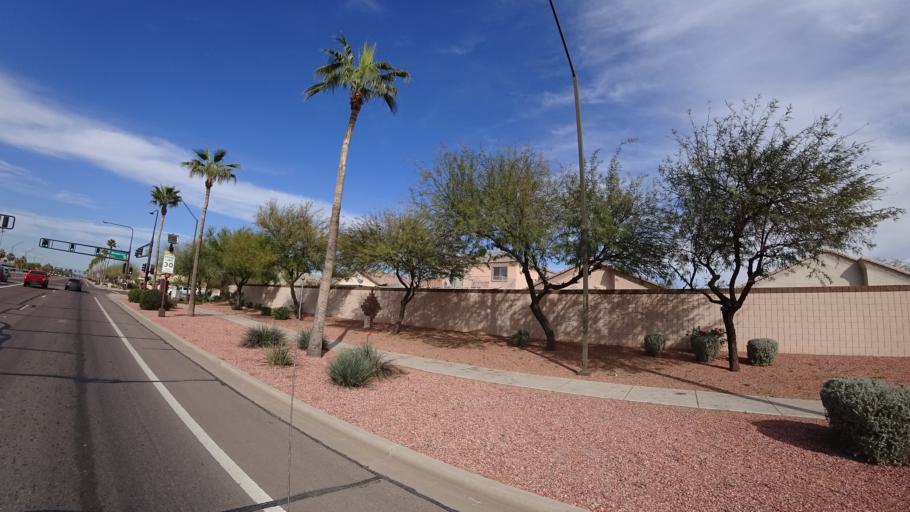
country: US
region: Arizona
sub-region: Maricopa County
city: Avondale
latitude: 33.4237
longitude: -112.3063
